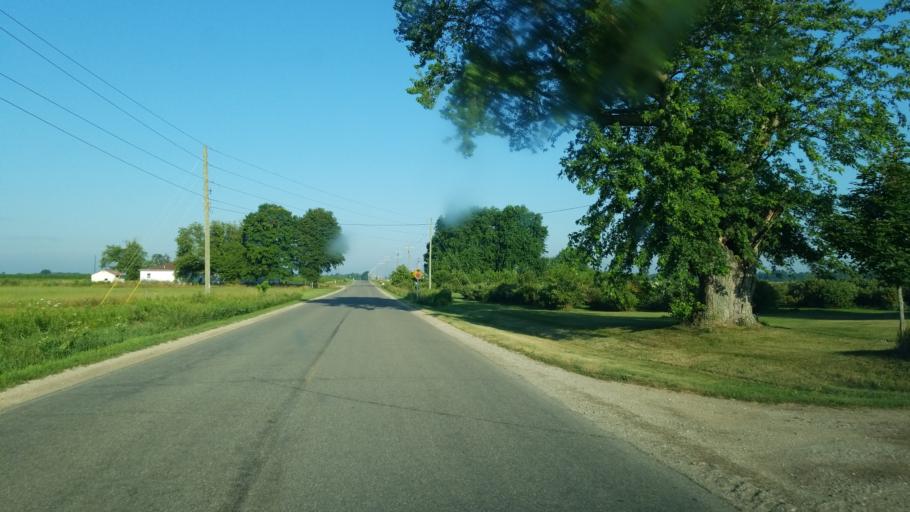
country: US
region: Michigan
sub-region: Mecosta County
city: Canadian Lakes
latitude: 43.5398
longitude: -85.2221
